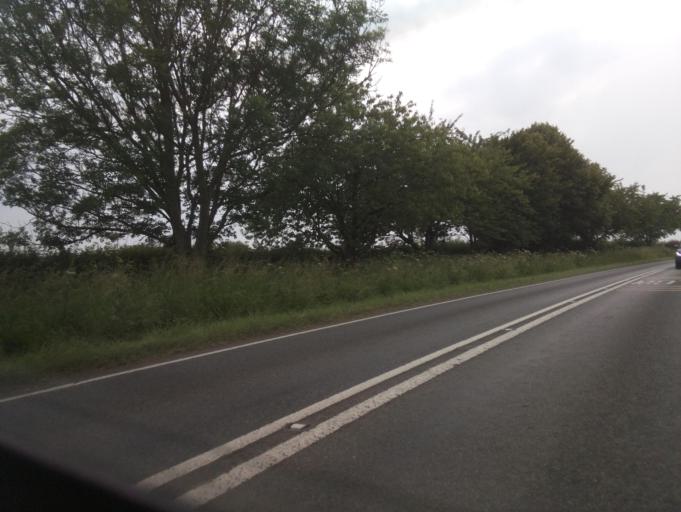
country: GB
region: England
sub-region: Somerset
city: Stoke-sub-Hamdon
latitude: 50.9112
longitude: -2.7262
